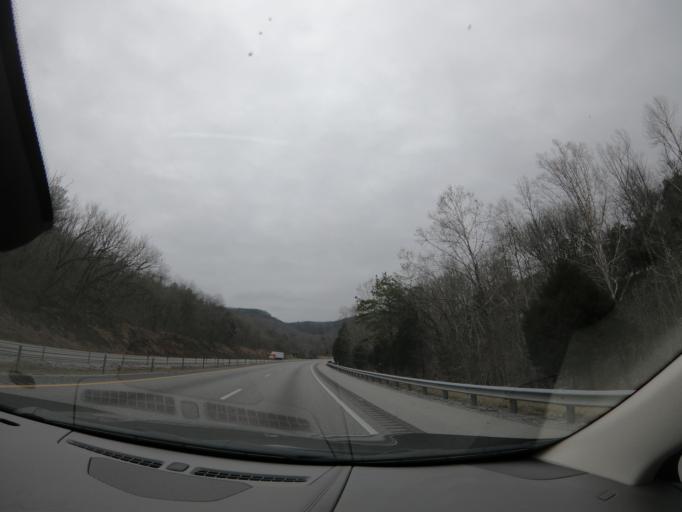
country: US
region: Georgia
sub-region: Dade County
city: Trenton
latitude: 34.9873
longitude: -85.5025
